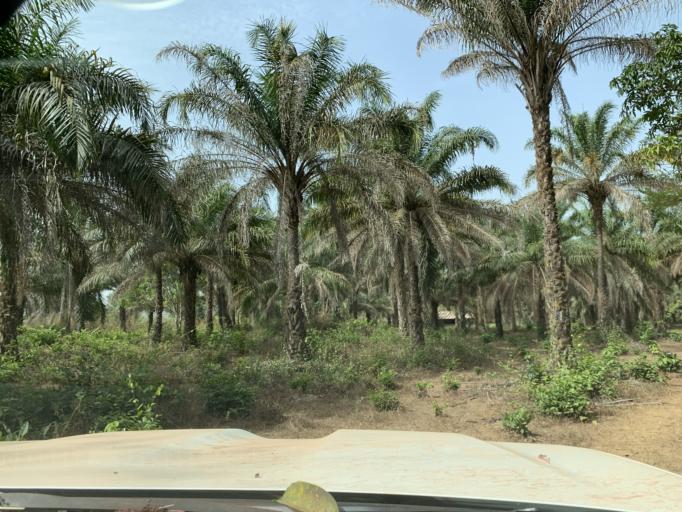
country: GN
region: Kindia
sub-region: Kindia
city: Kindia
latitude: 9.9732
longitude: -12.9837
